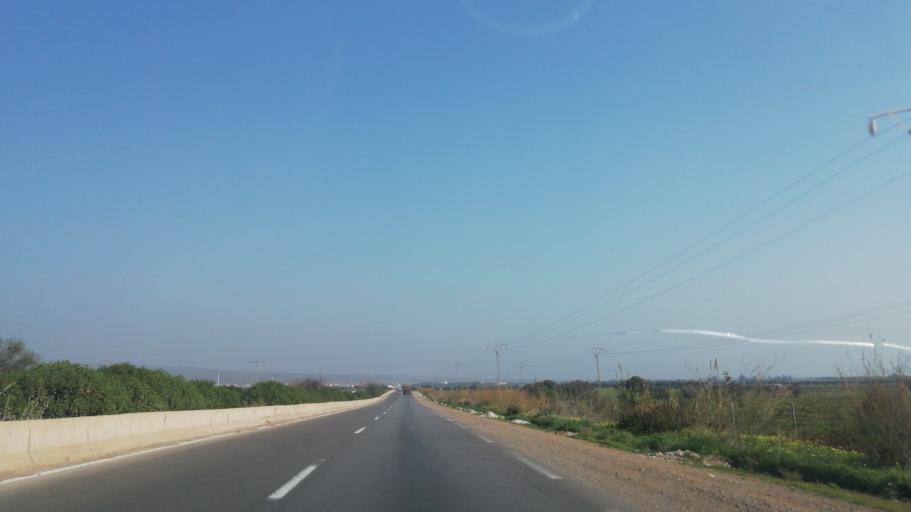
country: DZ
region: Oran
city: Bou Tlelis
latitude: 35.5620
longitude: -0.9269
